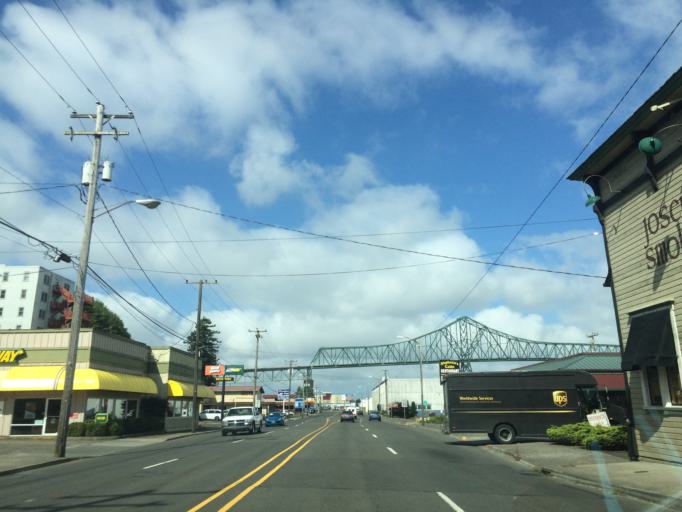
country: US
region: Oregon
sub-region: Clatsop County
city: Astoria
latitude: 46.1906
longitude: -123.8414
